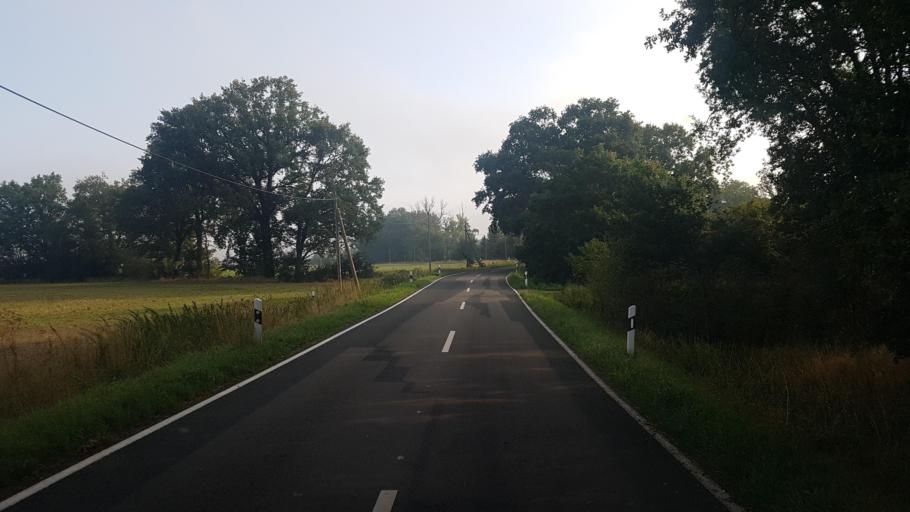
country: DE
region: Saxony-Anhalt
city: Pretzsch
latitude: 51.7356
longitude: 12.8290
